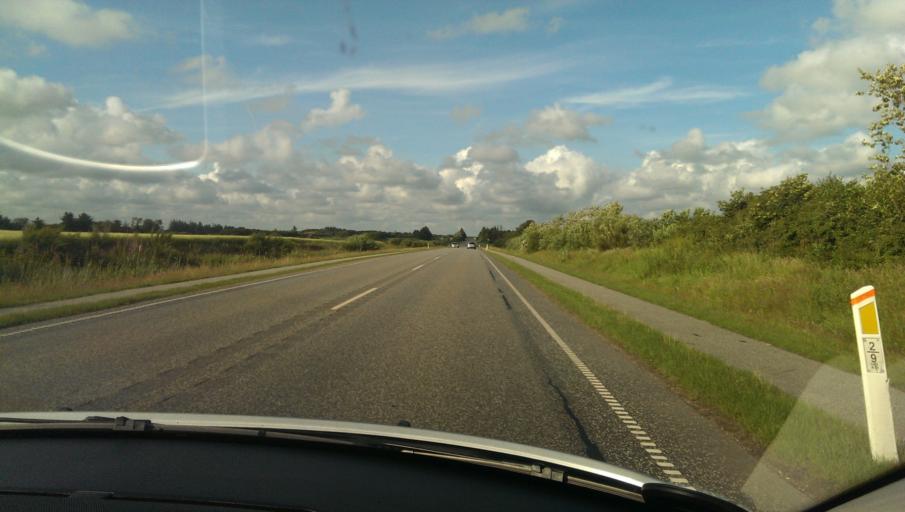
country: DK
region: Central Jutland
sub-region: Ringkobing-Skjern Kommune
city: Ringkobing
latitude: 56.1127
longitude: 8.2662
